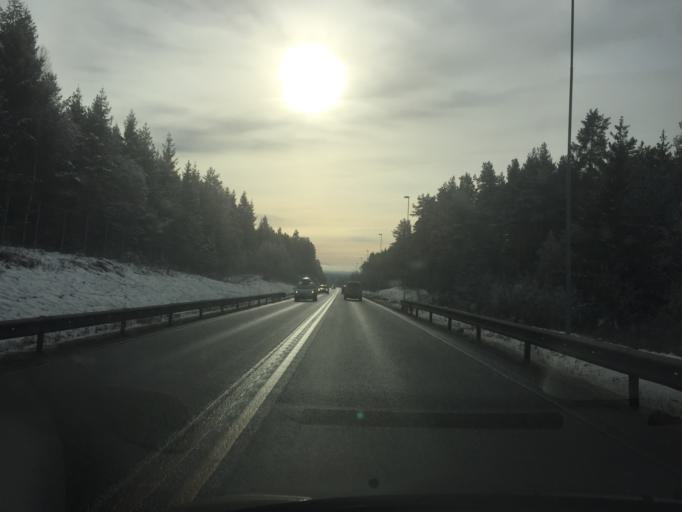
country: NO
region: Hedmark
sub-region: Loten
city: Loten
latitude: 60.7476
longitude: 11.3005
